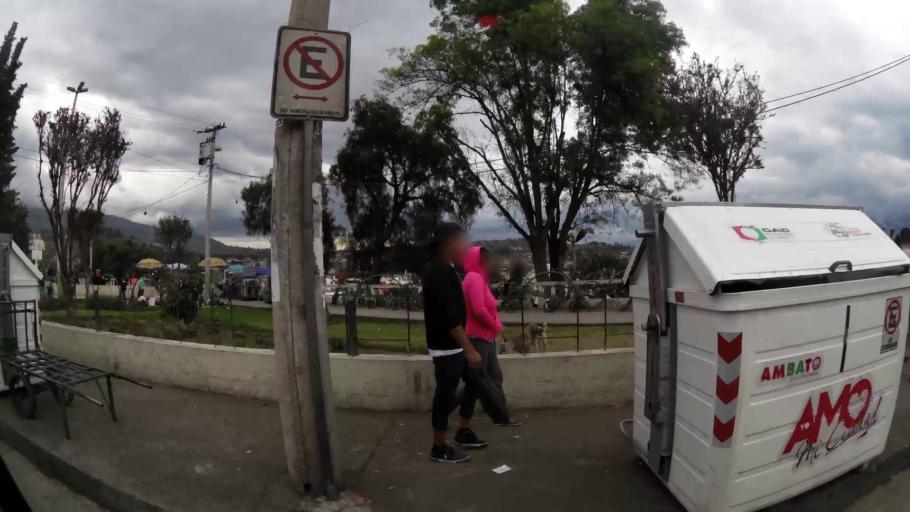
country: EC
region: Tungurahua
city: Ambato
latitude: -1.2366
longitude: -78.6174
